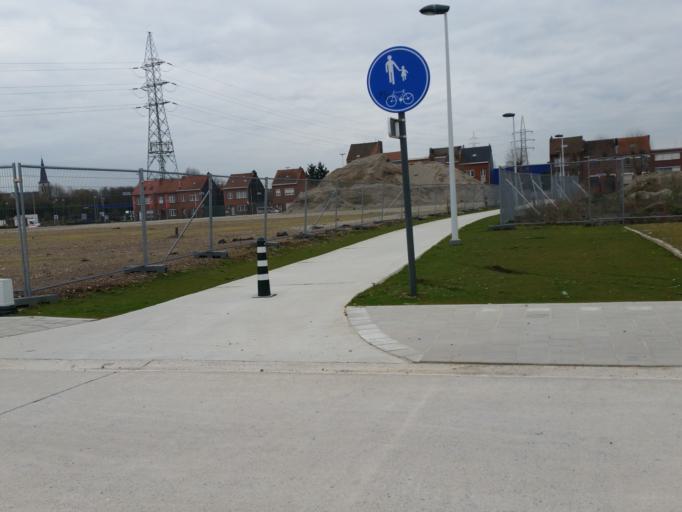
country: BE
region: Flanders
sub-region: Provincie Vlaams-Brabant
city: Vilvoorde
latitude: 50.9180
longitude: 4.4324
